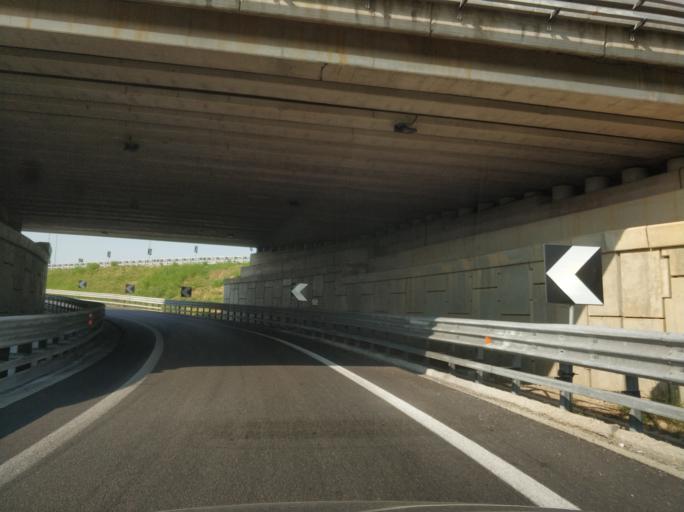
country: IT
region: Piedmont
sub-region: Provincia di Cuneo
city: Roreto
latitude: 44.6640
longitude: 7.8097
